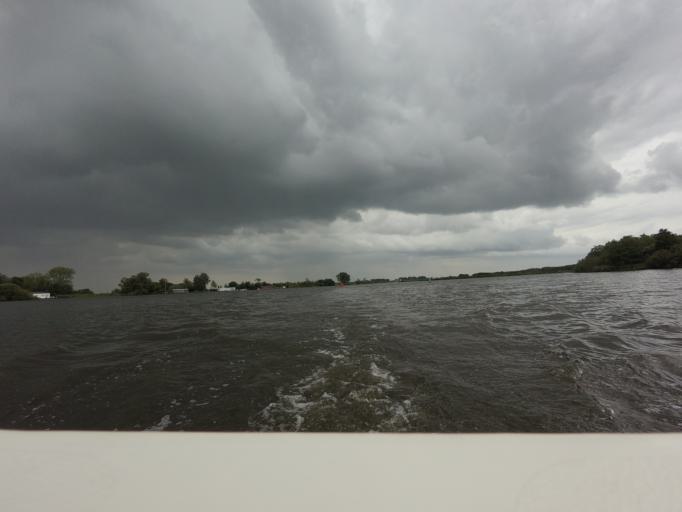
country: NL
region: Friesland
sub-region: Gemeente Tytsjerksteradiel
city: Garyp
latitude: 53.1203
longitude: 5.9444
